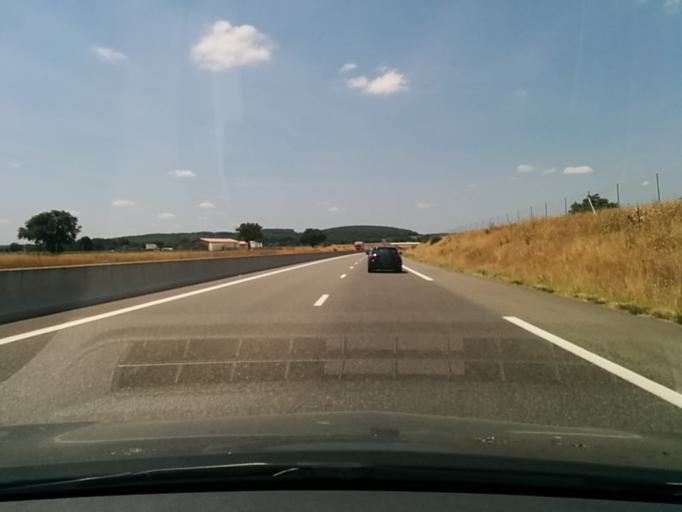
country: FR
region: Midi-Pyrenees
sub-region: Departement de la Haute-Garonne
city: Fontenilles
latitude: 43.5811
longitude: 1.1965
